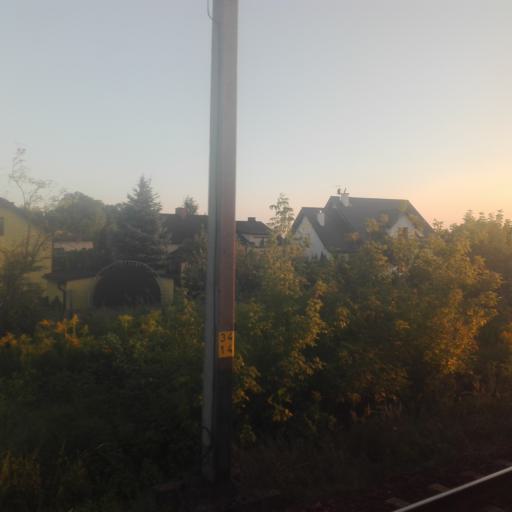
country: PL
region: Masovian Voivodeship
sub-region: Powiat warszawski zachodni
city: Bieniewice
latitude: 52.1899
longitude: 20.5249
